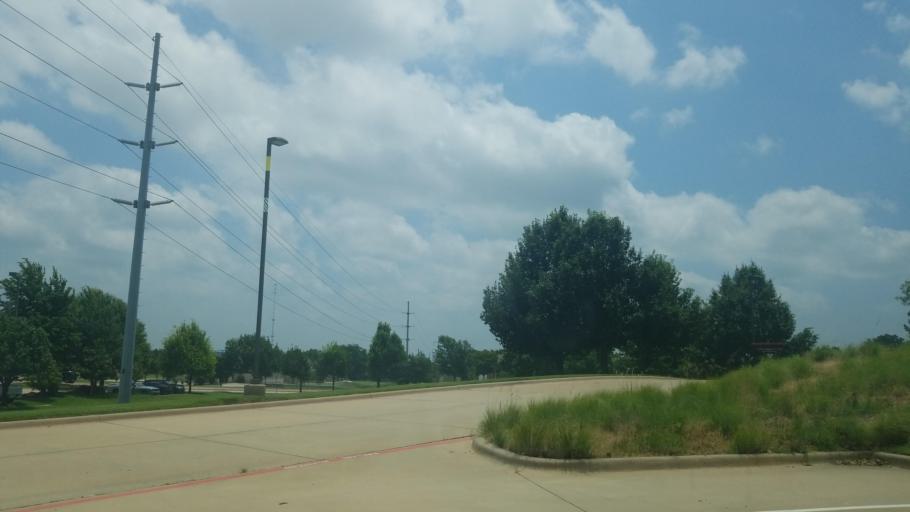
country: US
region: Texas
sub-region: Denton County
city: Corinth
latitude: 33.1850
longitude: -97.0982
